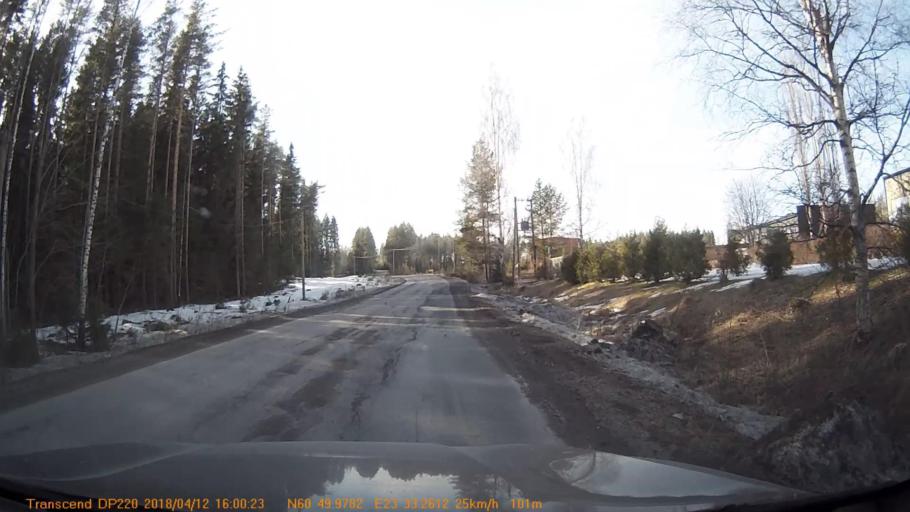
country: FI
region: Haeme
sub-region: Forssa
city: Forssa
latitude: 60.8331
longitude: 23.5539
